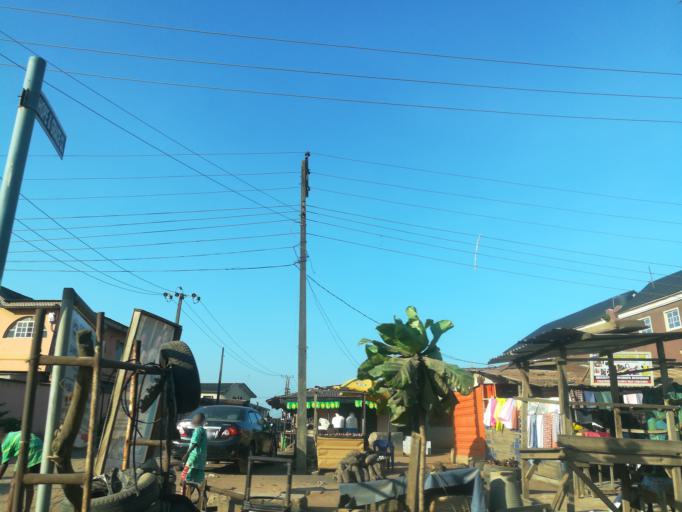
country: NG
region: Lagos
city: Ikorodu
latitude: 6.5870
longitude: 3.5208
